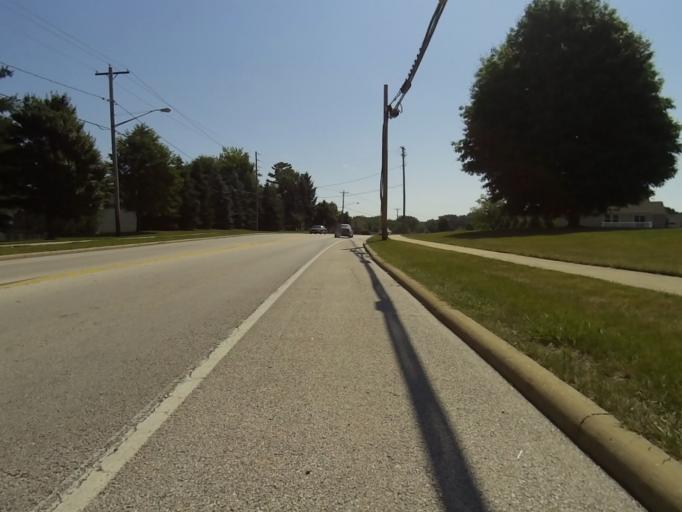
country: US
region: Ohio
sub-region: Portage County
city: Kent
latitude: 41.1644
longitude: -81.3781
